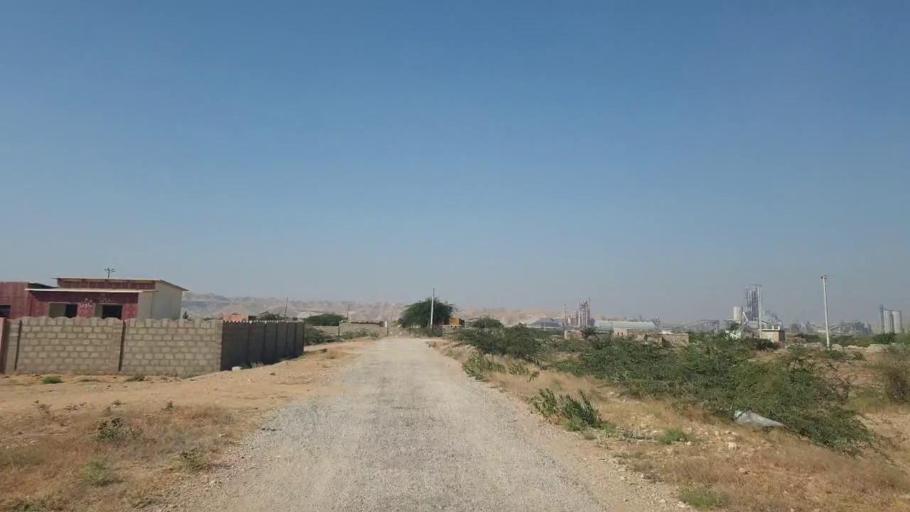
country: PK
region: Sindh
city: Gharo
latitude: 25.1478
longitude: 67.7231
